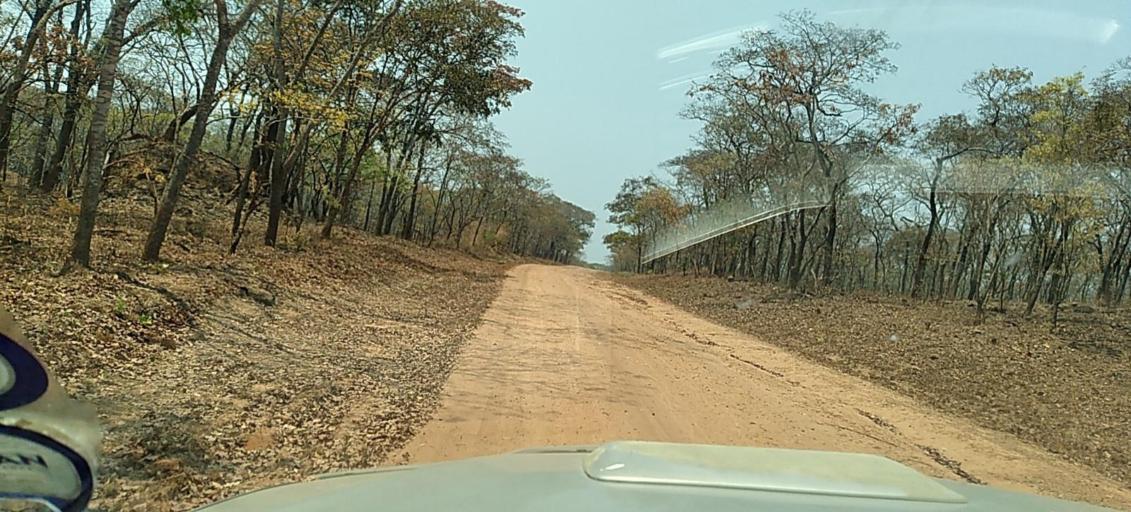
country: ZM
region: North-Western
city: Kasempa
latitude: -13.5540
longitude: 26.0666
